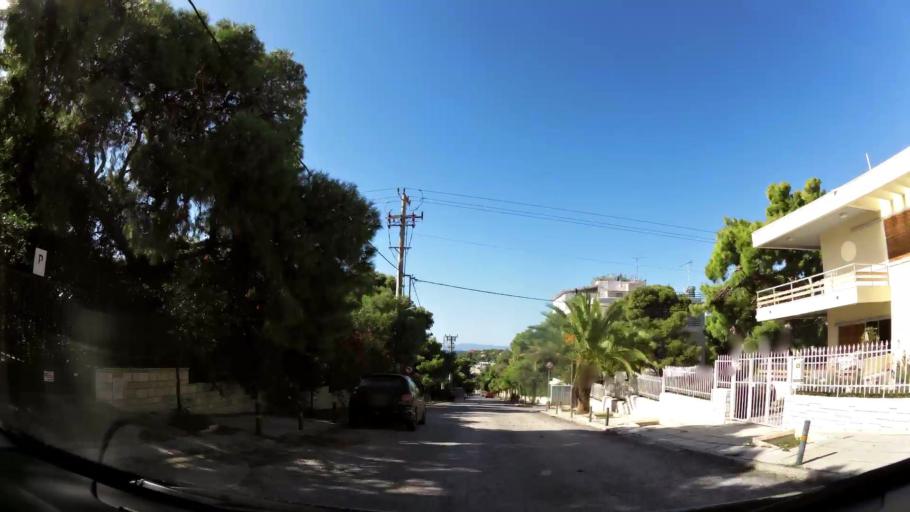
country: GR
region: Attica
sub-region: Nomarchia Anatolikis Attikis
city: Vouliagmeni
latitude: 37.8149
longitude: 23.7840
